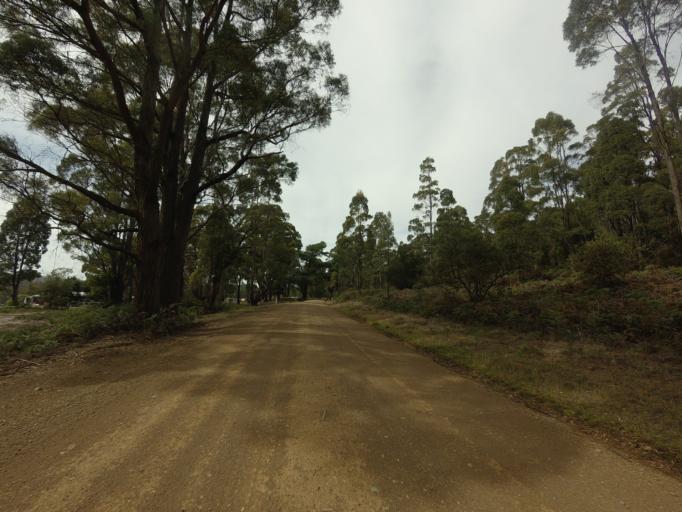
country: AU
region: Tasmania
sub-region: Sorell
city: Sorell
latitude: -42.4961
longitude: 147.6294
